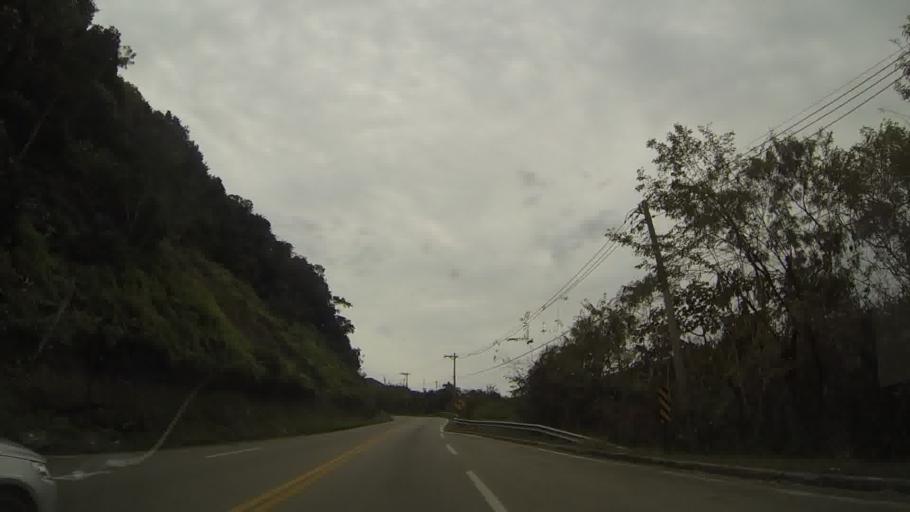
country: BR
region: Sao Paulo
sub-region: Sao Sebastiao
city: Sao Sebastiao
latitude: -23.8249
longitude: -45.4481
